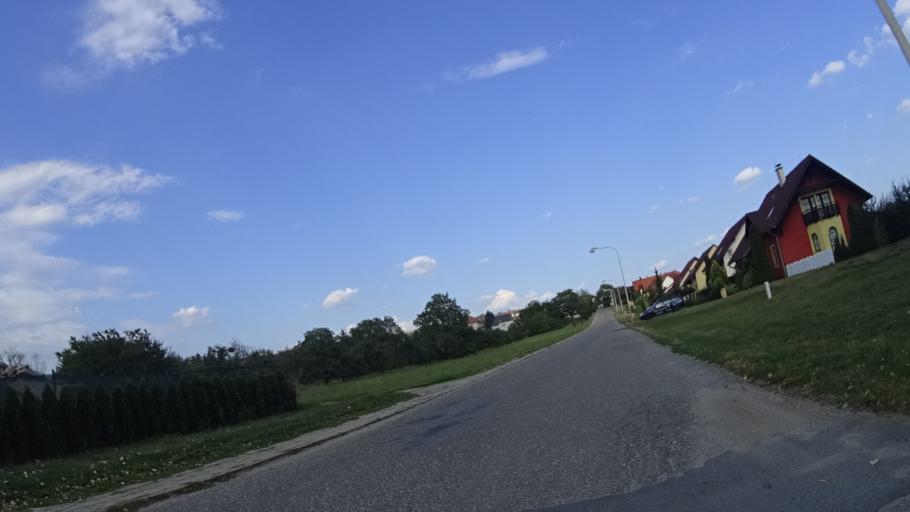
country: CZ
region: Zlin
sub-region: Okres Zlin
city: Napajedla
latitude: 49.1606
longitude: 17.5120
